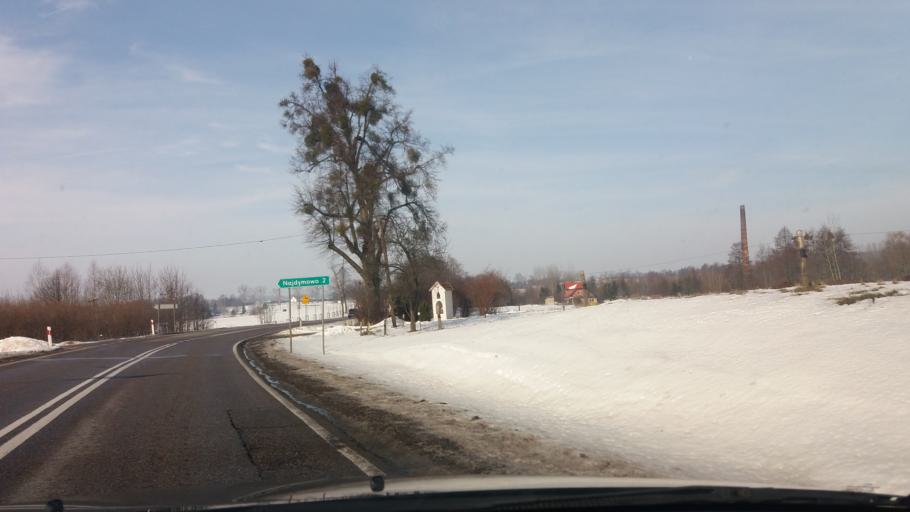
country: PL
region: Warmian-Masurian Voivodeship
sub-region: Powiat olsztynski
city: Biskupiec
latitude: 53.8840
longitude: 20.9220
